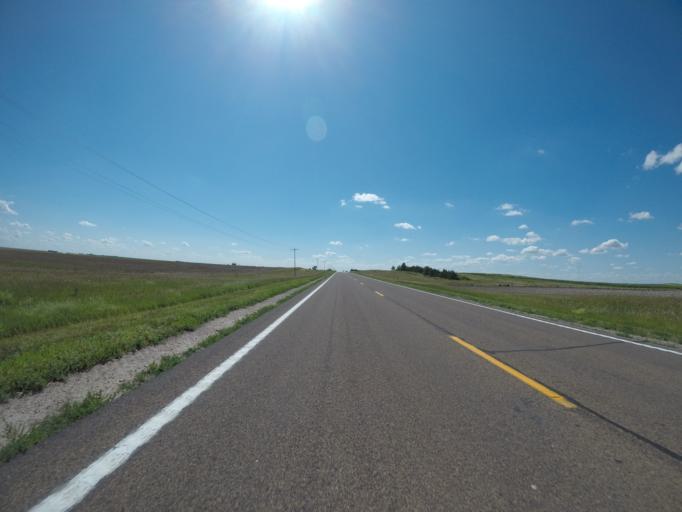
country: US
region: Nebraska
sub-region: Chase County
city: Imperial
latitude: 40.5375
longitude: -101.8268
